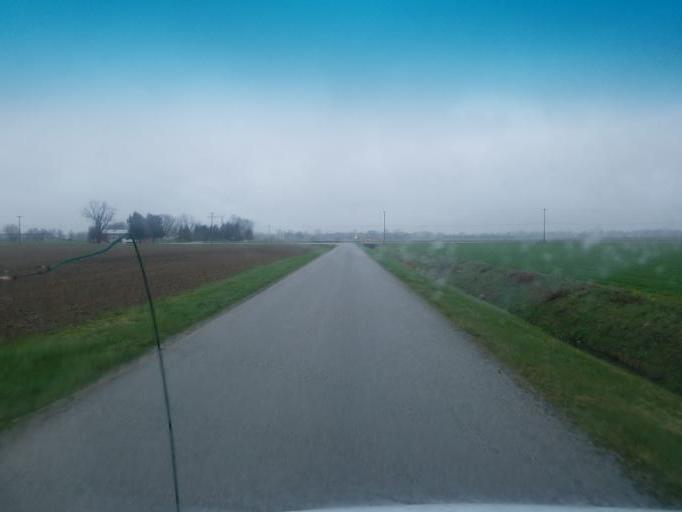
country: US
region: Ohio
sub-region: Wood County
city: North Baltimore
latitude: 41.2555
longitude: -83.6314
